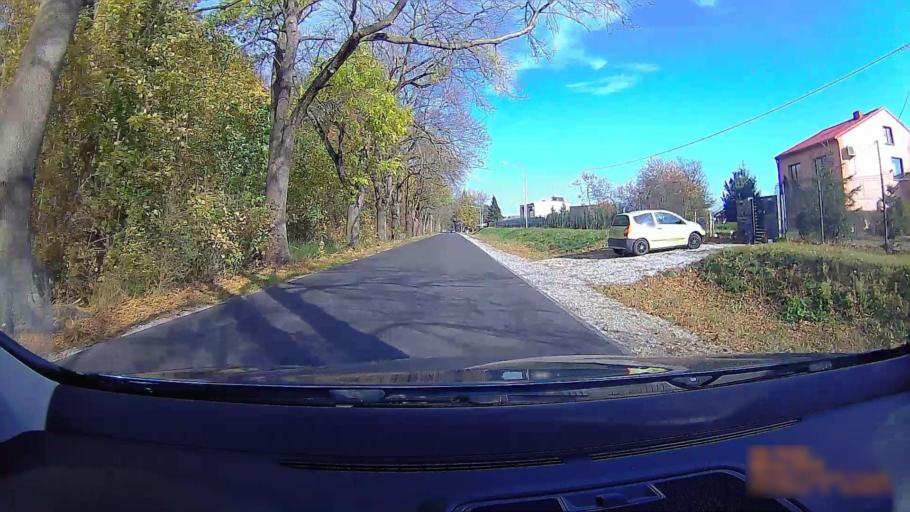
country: PL
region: Greater Poland Voivodeship
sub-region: Powiat ostrzeszowski
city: Doruchow
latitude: 51.3950
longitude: 18.0585
